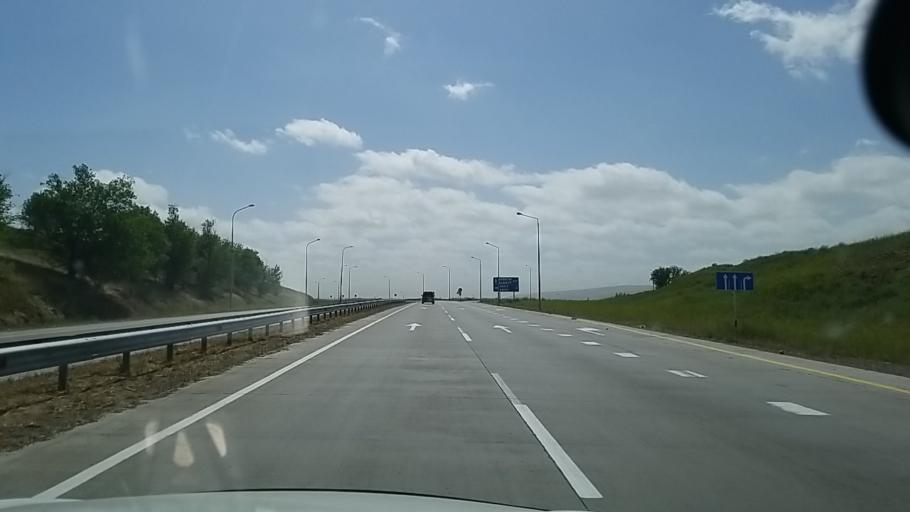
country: KZ
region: Ongtustik Qazaqstan
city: Aksu
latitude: 42.4736
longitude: 69.8955
